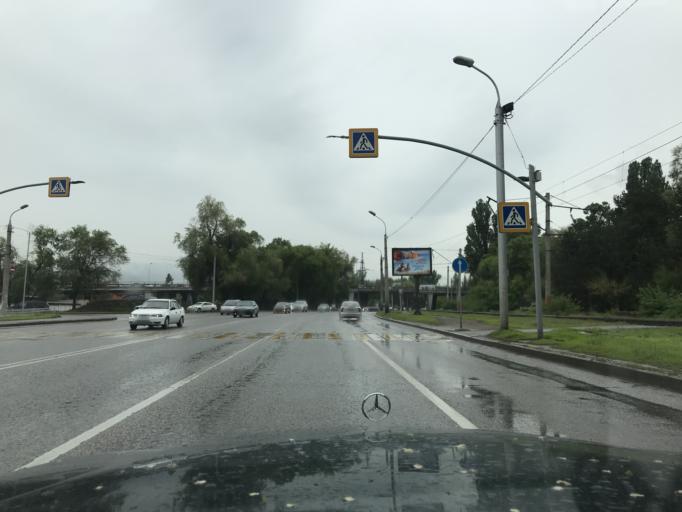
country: KZ
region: Almaty Qalasy
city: Almaty
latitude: 43.2961
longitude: 76.9485
